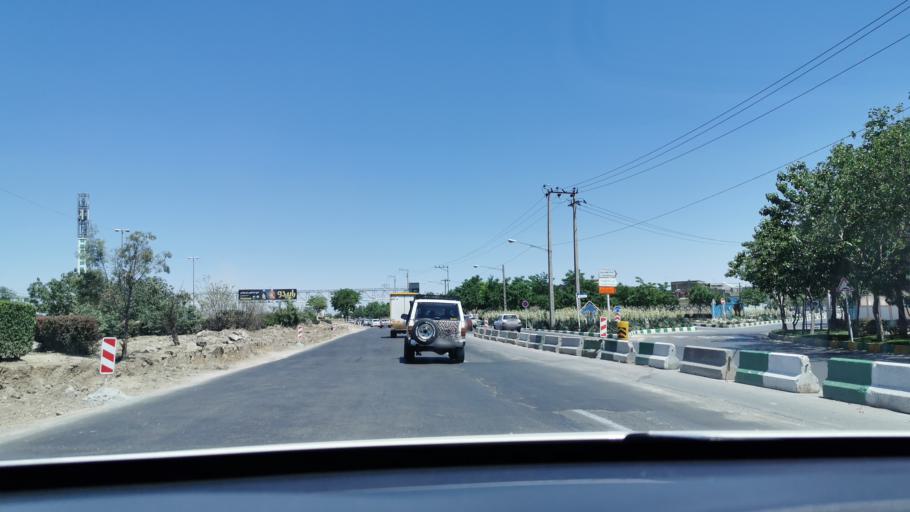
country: IR
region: Razavi Khorasan
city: Mashhad
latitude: 36.2587
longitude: 59.6411
